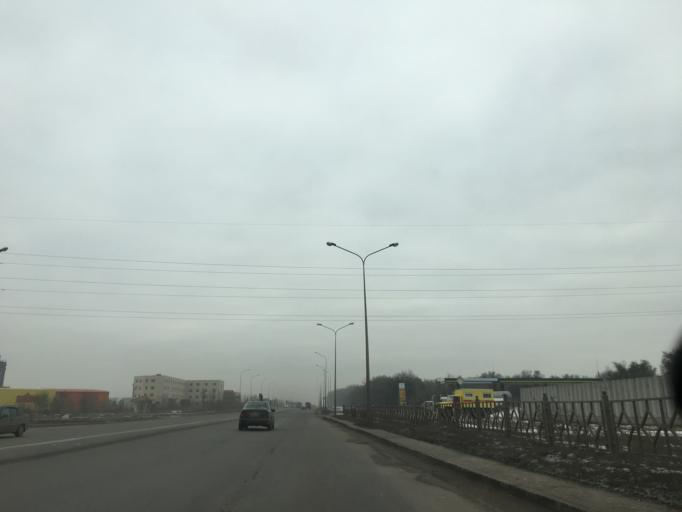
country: KZ
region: Astana Qalasy
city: Astana
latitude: 51.1708
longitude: 71.4906
